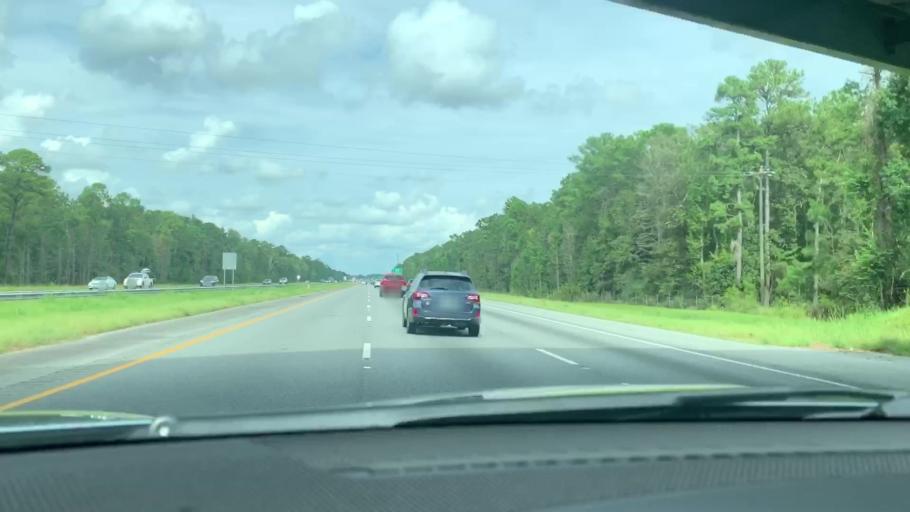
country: US
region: Georgia
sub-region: Liberty County
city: Midway
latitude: 31.6340
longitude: -81.4047
